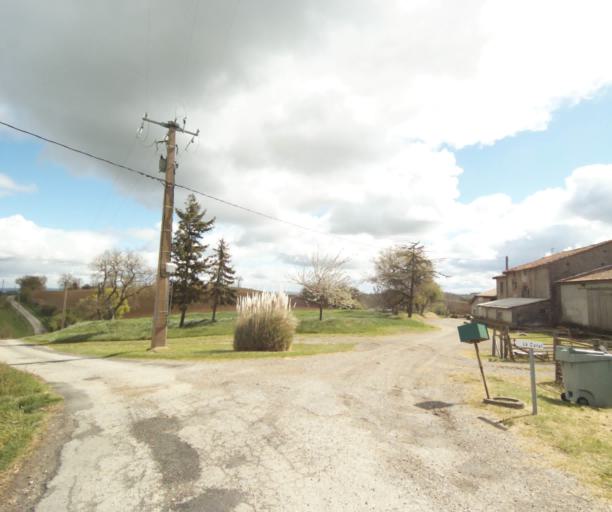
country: FR
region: Midi-Pyrenees
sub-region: Departement de l'Ariege
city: Saverdun
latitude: 43.1933
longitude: 1.5460
